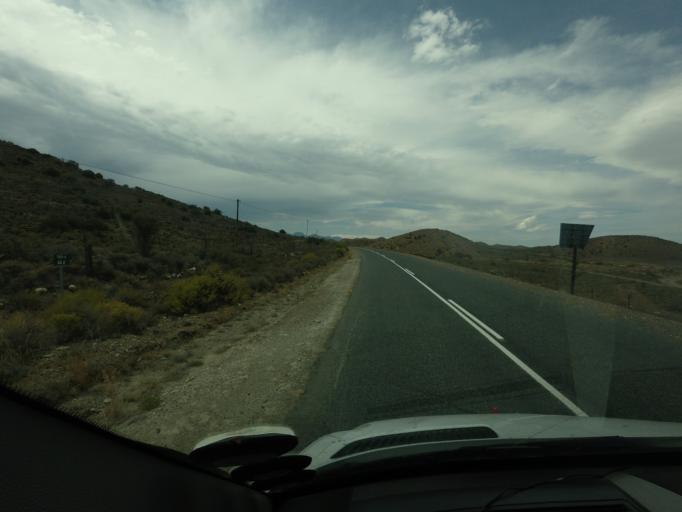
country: ZA
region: Western Cape
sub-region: Eden District Municipality
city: Ladismith
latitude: -33.6443
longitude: 21.0295
